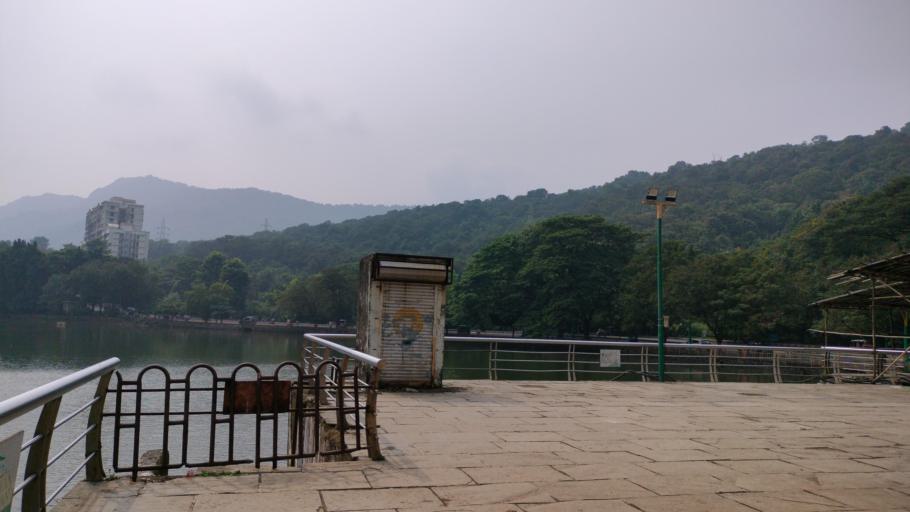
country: IN
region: Maharashtra
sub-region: Thane
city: Thane
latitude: 19.2223
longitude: 72.9562
